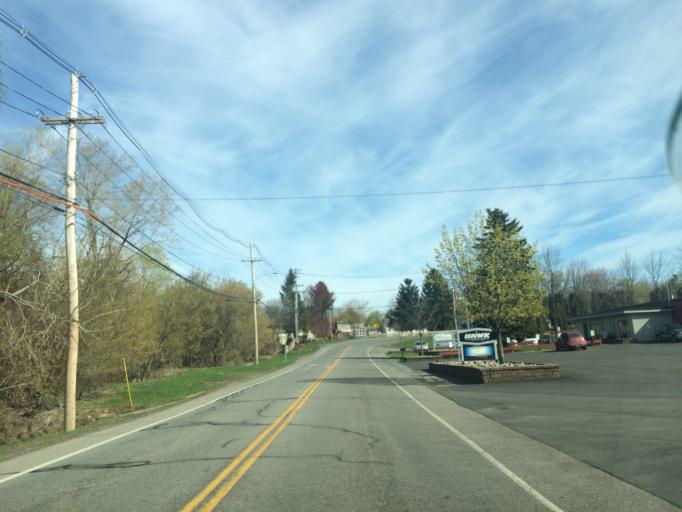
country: US
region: New York
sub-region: Monroe County
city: Fairport
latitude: 43.1041
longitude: -77.4555
